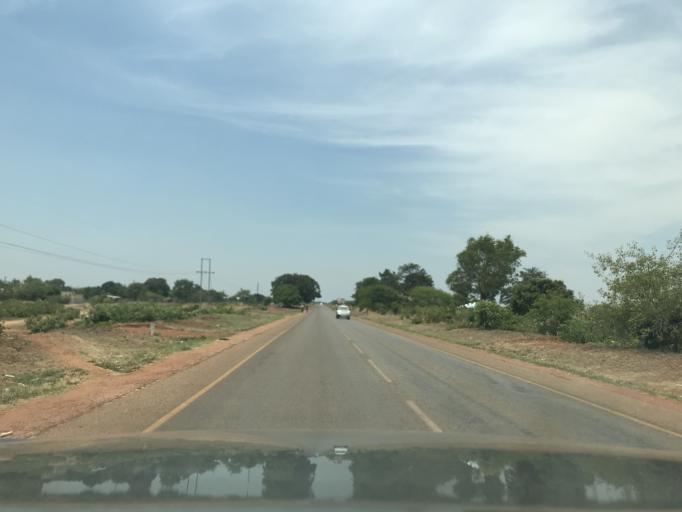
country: ZM
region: Northern
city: Kasama
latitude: -10.2161
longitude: 31.1484
